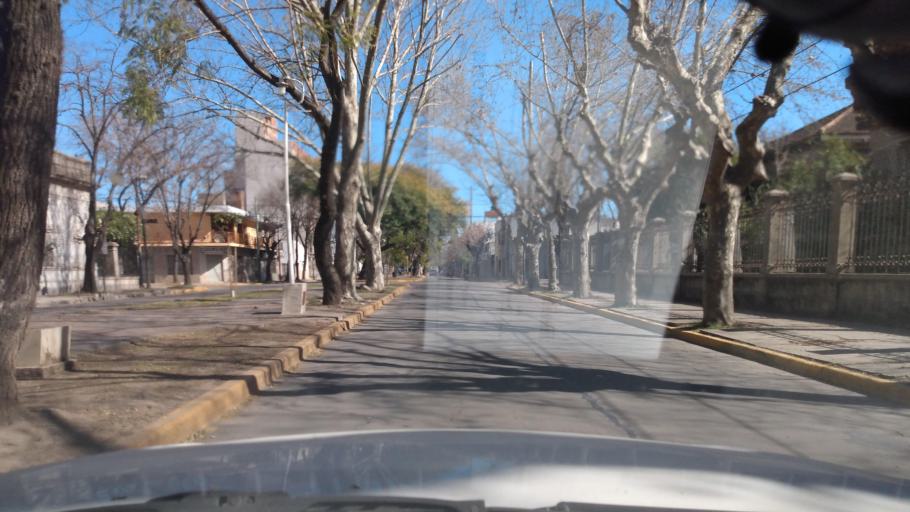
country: AR
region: Buenos Aires
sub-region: Partido de Mercedes
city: Mercedes
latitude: -34.6497
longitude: -59.4263
